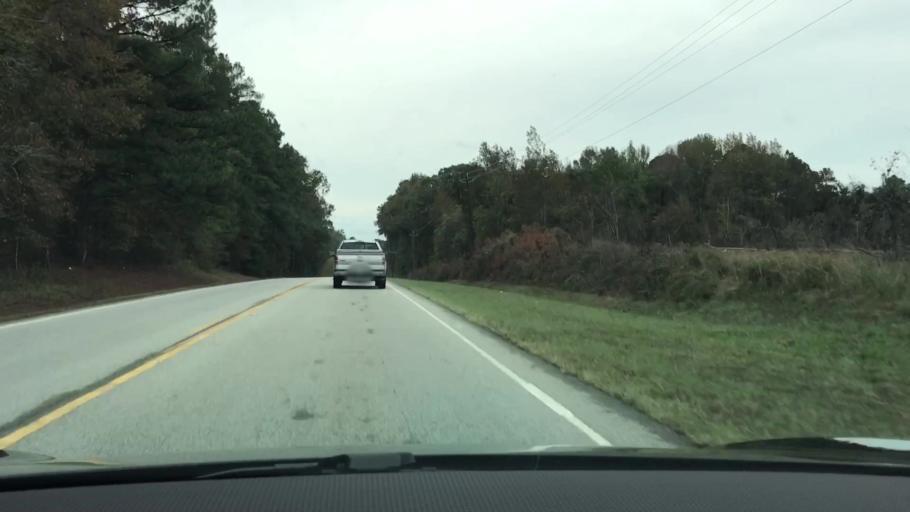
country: US
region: Georgia
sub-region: Warren County
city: Firing Range
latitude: 33.4343
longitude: -82.6881
